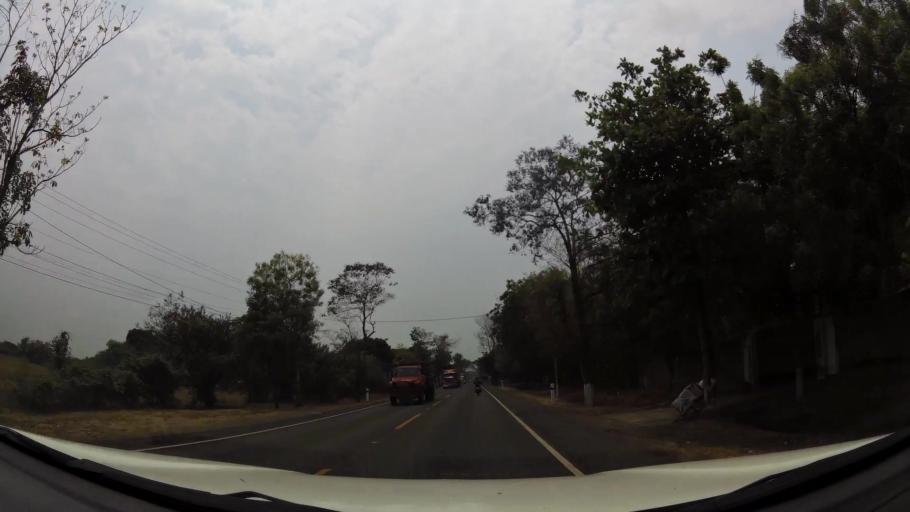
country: NI
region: Chinandega
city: Chichigalpa
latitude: 12.6088
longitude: -87.0722
